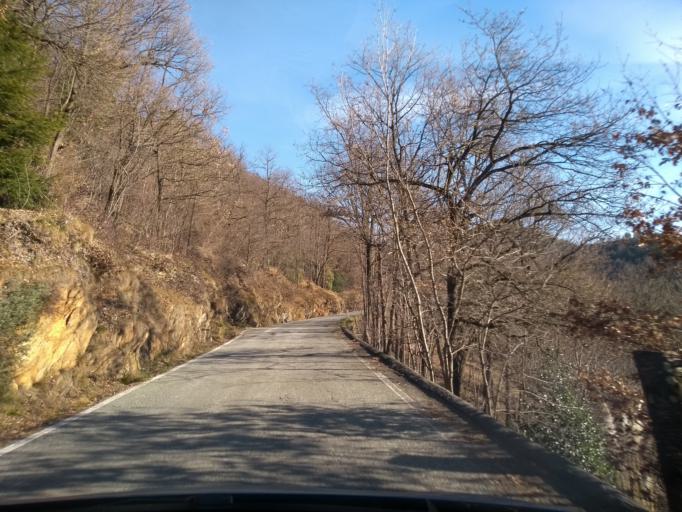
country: IT
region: Piedmont
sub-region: Provincia di Torino
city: Pessinetto
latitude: 45.2825
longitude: 7.4266
